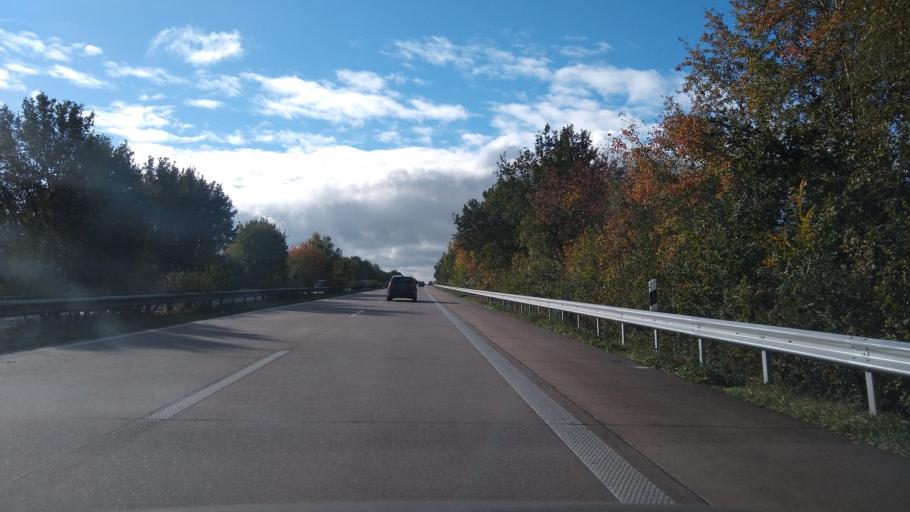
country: DE
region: Lower Saxony
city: Wardenburg
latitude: 52.9965
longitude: 8.2034
